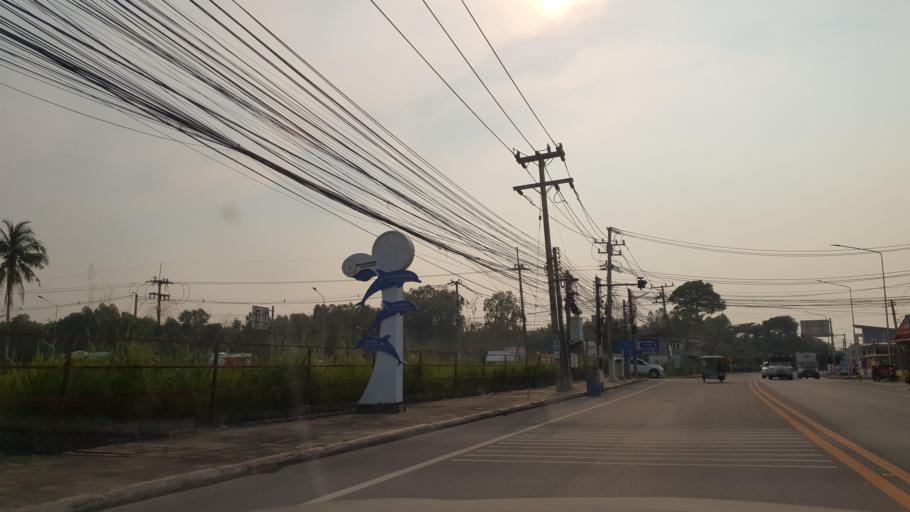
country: TH
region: Rayong
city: Rayong
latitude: 12.6154
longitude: 101.4172
